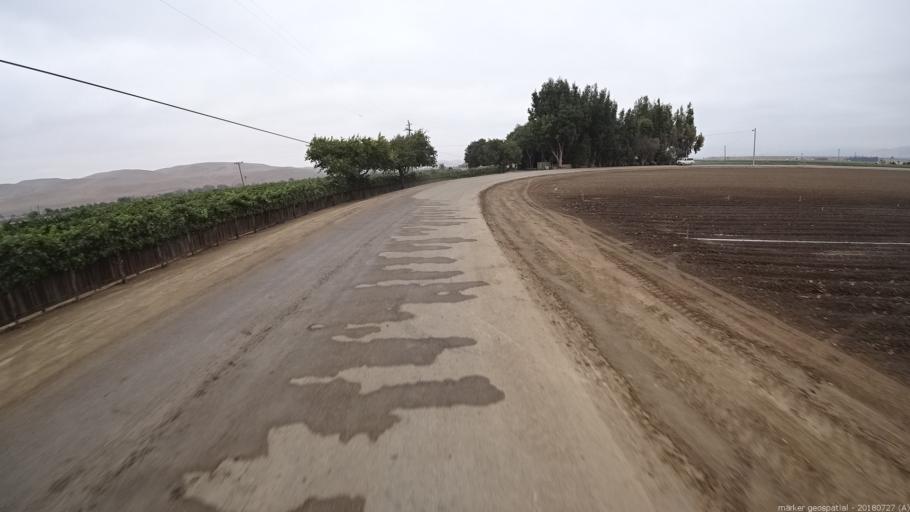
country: US
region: California
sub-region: Monterey County
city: Greenfield
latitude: 36.3243
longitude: -121.2031
